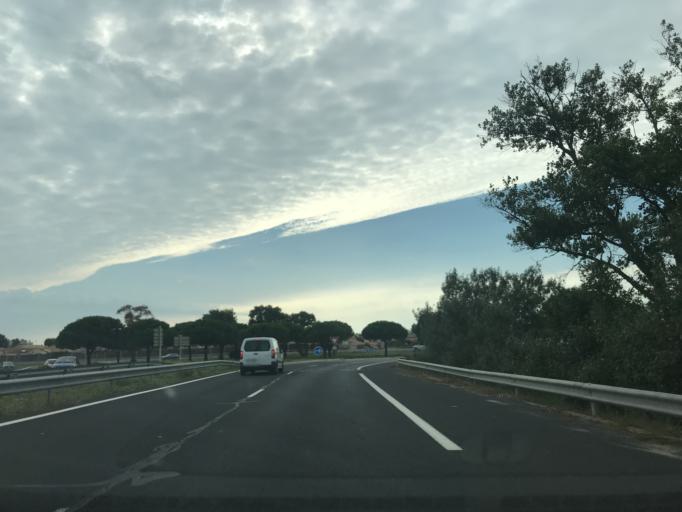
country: FR
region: Languedoc-Roussillon
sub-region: Departement du Gard
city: Le Grau-du-Roi
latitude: 43.5493
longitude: 4.1354
